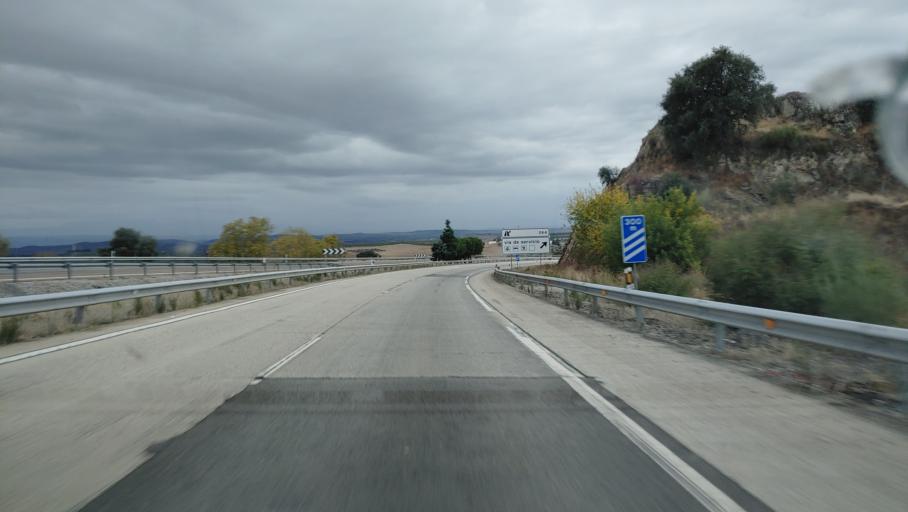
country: ES
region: Andalusia
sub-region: Provincia de Jaen
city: La Carolina
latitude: 38.3026
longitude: -3.5790
